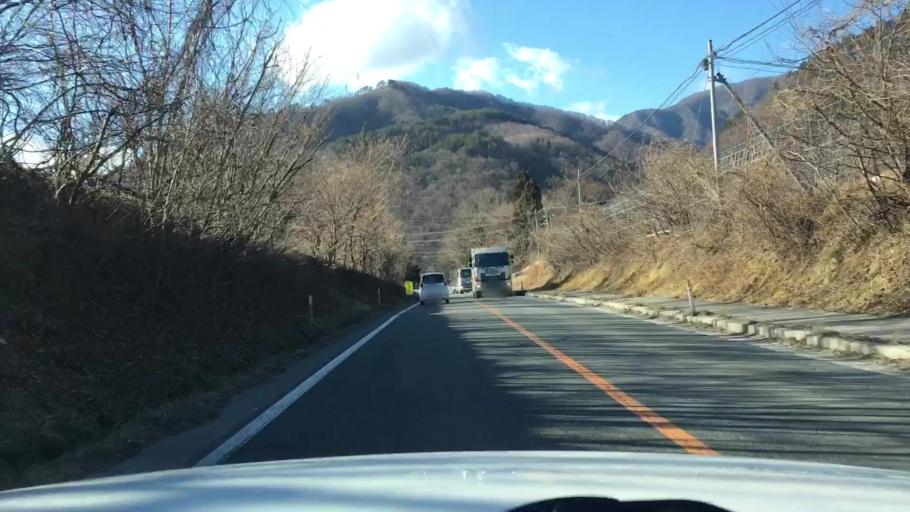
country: JP
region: Iwate
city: Miyako
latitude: 39.6027
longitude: 141.7707
